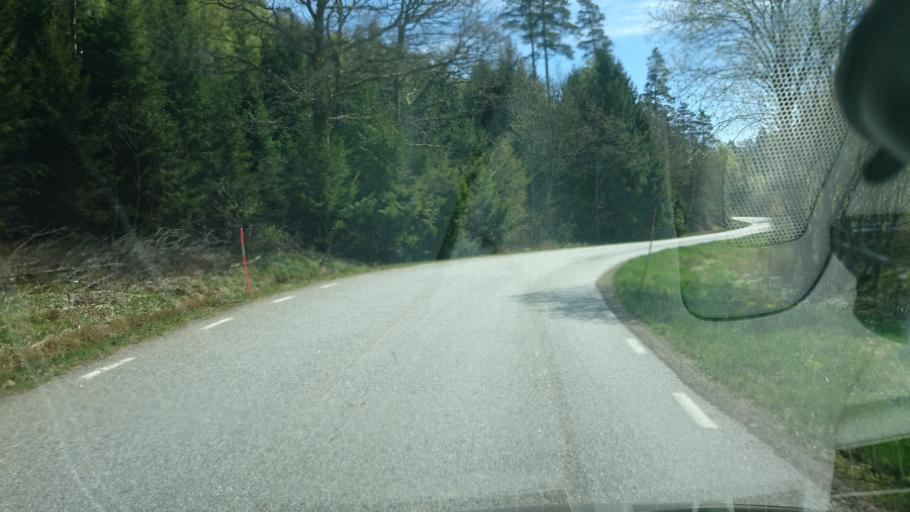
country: SE
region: Vaestra Goetaland
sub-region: Munkedals Kommun
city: Munkedal
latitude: 58.3711
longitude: 11.6904
